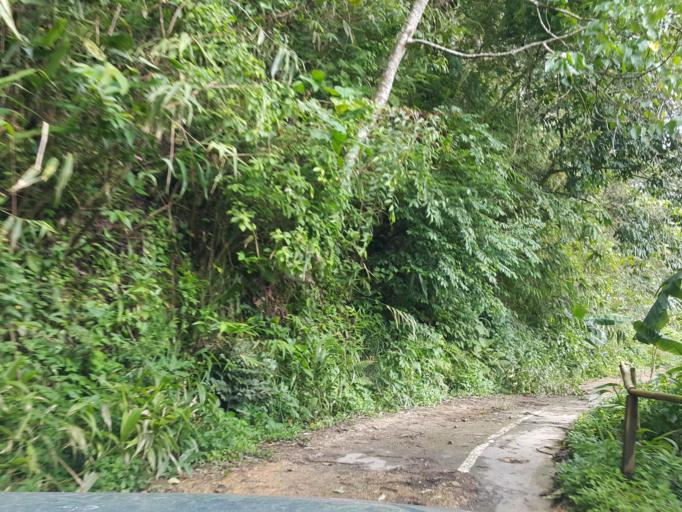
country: TH
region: Tak
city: Tak
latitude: 16.7821
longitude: 98.9271
